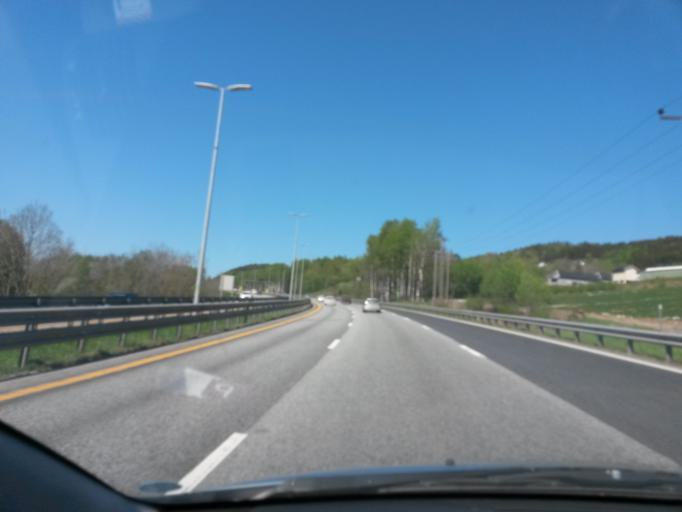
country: NO
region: Buskerud
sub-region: Lier
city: Lierbyen
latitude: 59.7781
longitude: 10.2771
